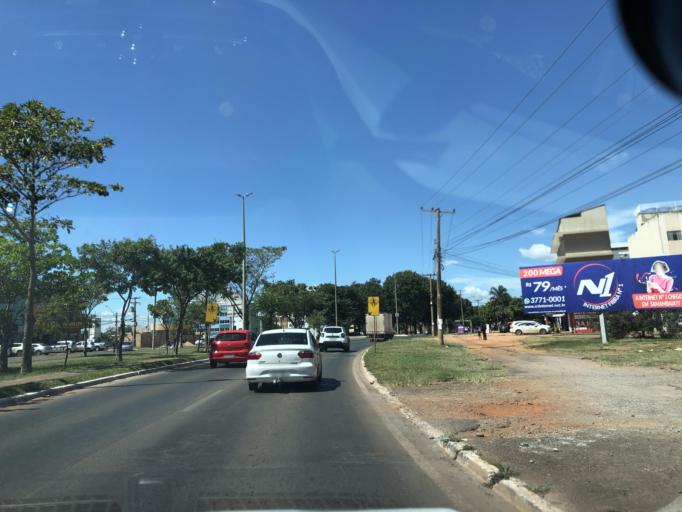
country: BR
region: Federal District
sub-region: Brasilia
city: Brasilia
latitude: -15.8706
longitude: -48.0614
